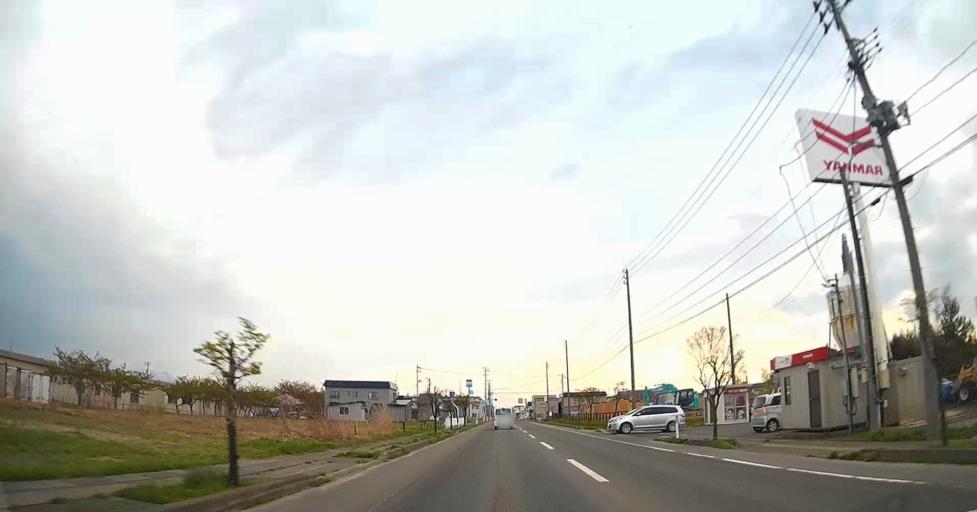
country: JP
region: Aomori
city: Aomori Shi
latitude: 40.8610
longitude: 140.6812
